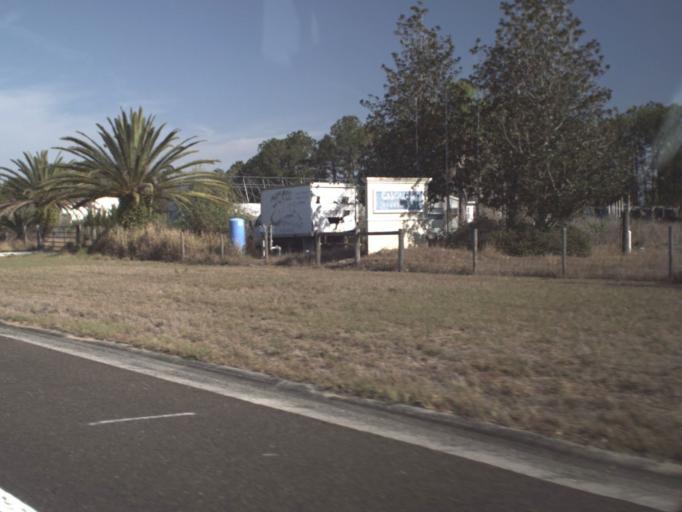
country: US
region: Florida
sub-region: Lake County
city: Minneola
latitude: 28.6352
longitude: -81.7802
